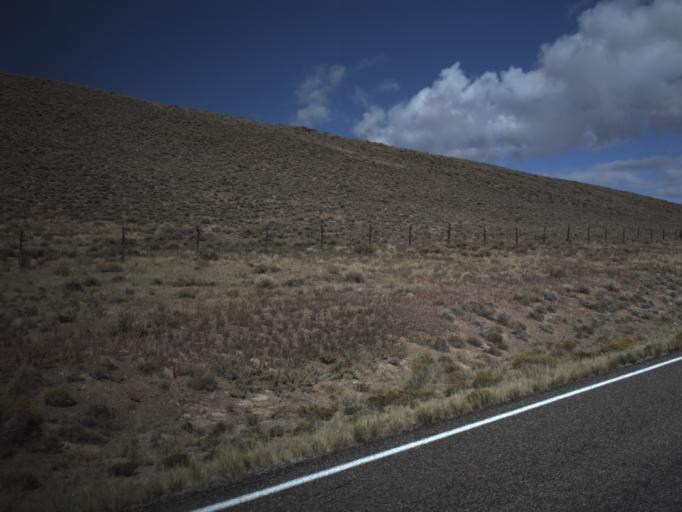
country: US
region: Utah
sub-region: Beaver County
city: Milford
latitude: 38.6064
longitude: -113.8349
